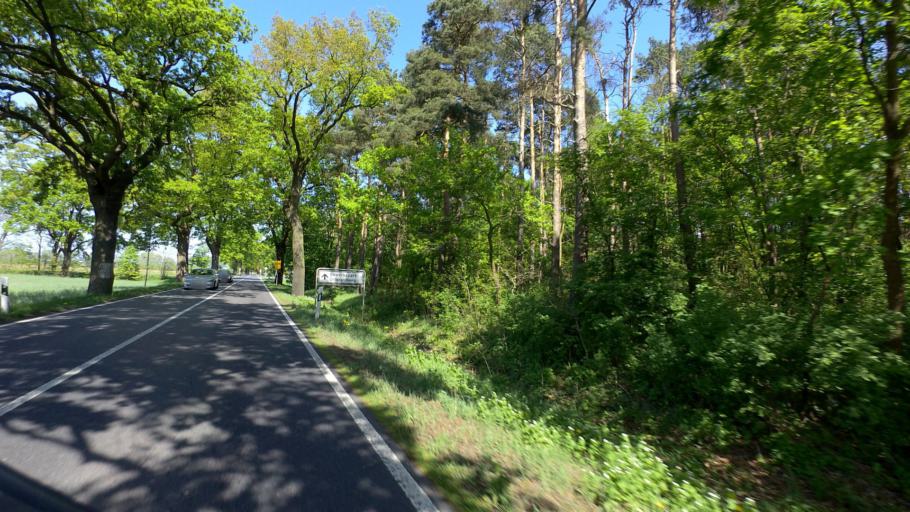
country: DE
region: Brandenburg
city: Beeskow
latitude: 52.1803
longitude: 14.2793
